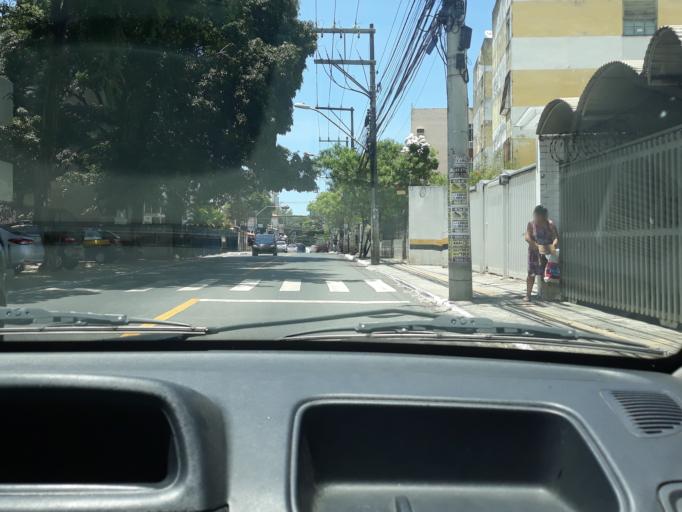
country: BR
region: Bahia
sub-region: Salvador
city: Salvador
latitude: -13.0012
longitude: -38.5019
